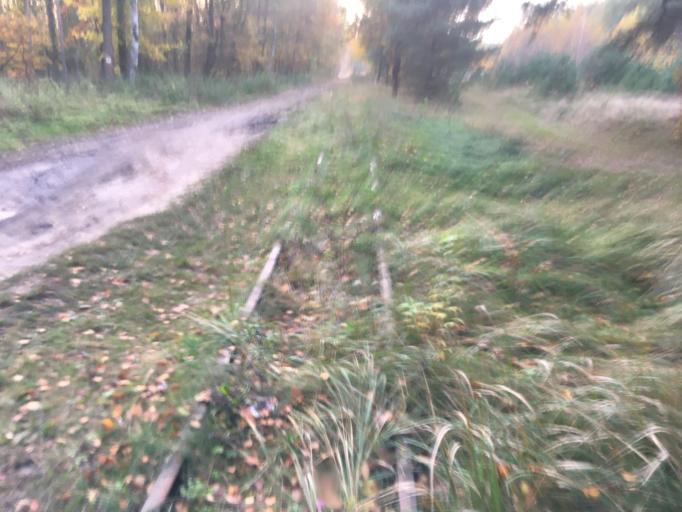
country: PL
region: Swietokrzyskie
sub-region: Powiat starachowicki
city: Starachowice
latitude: 51.0667
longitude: 21.1316
